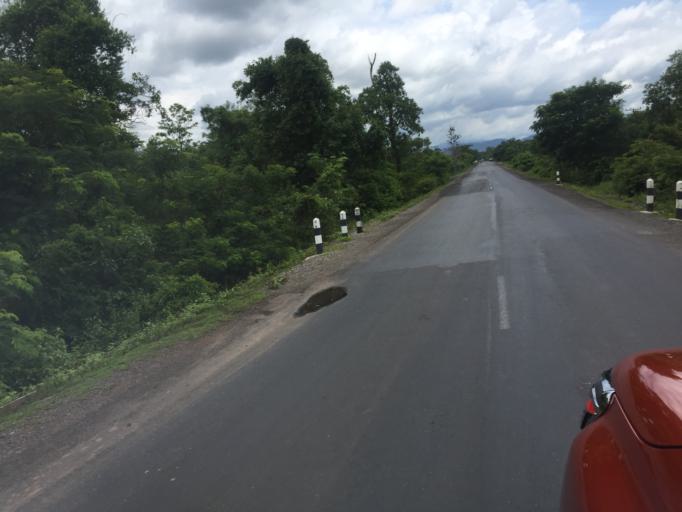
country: LA
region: Salavan
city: Salavan
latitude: 15.8374
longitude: 106.3882
